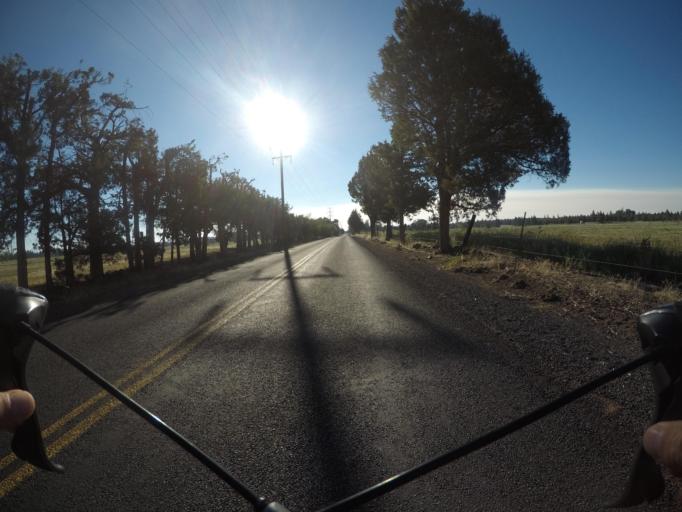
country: US
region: Oregon
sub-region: Deschutes County
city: Redmond
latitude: 44.2621
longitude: -121.2443
